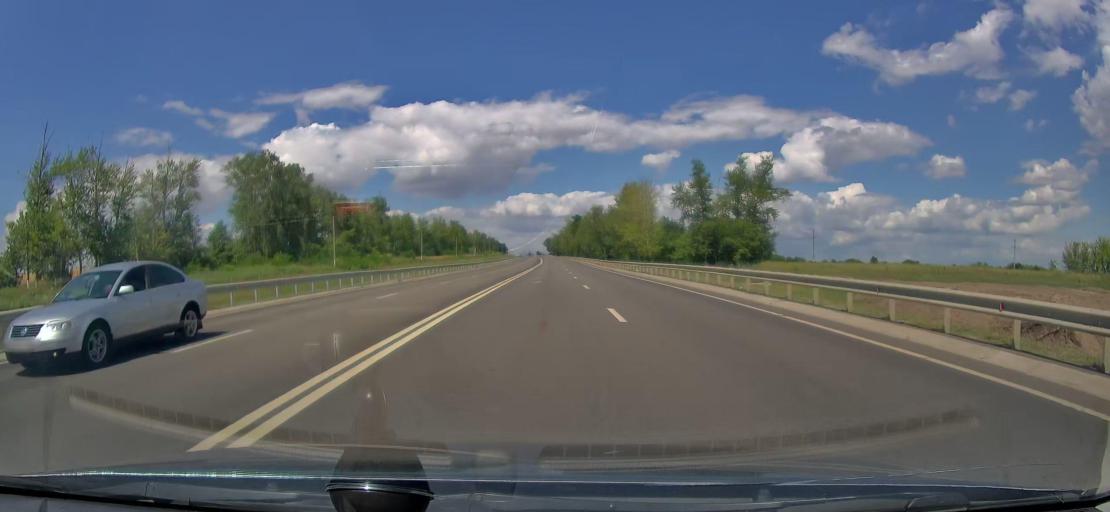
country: RU
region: Kursk
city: Zolotukhino
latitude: 51.9536
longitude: 36.3047
